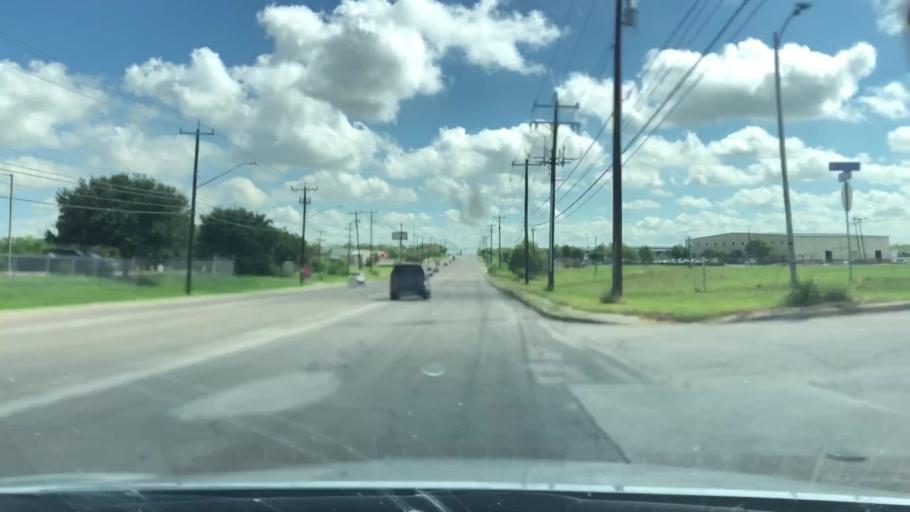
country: US
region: Texas
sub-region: Bexar County
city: Kirby
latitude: 29.4841
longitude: -98.3835
